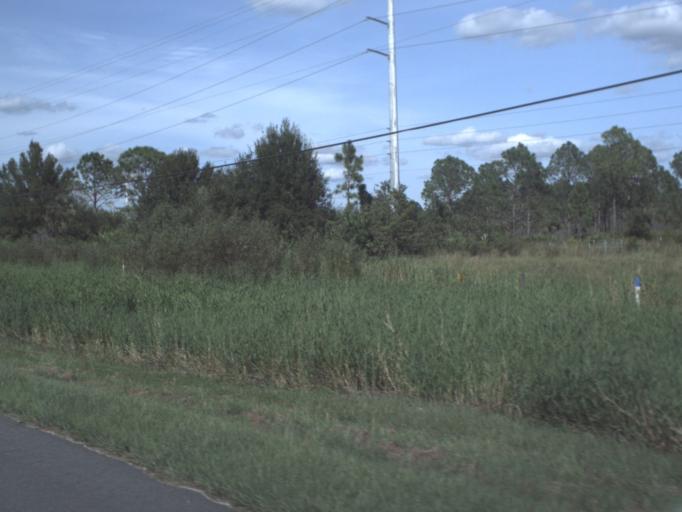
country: US
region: Florida
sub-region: Lee County
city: Fort Myers Shores
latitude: 26.8146
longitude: -81.7602
